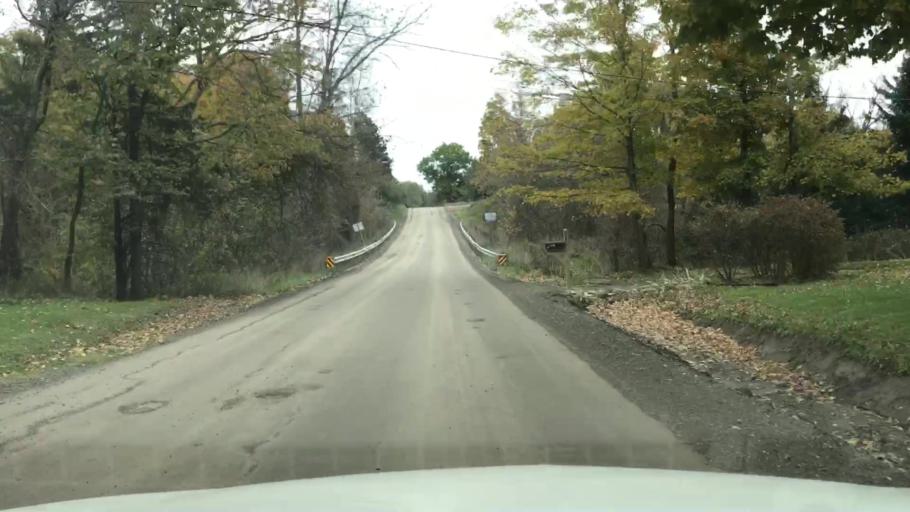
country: US
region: Michigan
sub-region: Oakland County
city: Rochester
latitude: 42.7335
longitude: -83.1196
